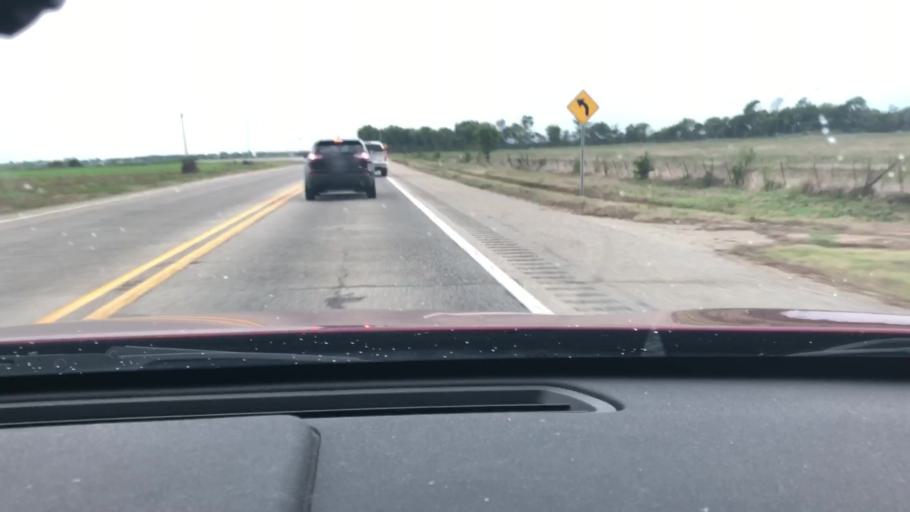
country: US
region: Arkansas
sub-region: Lafayette County
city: Lewisville
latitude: 33.4006
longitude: -93.7445
